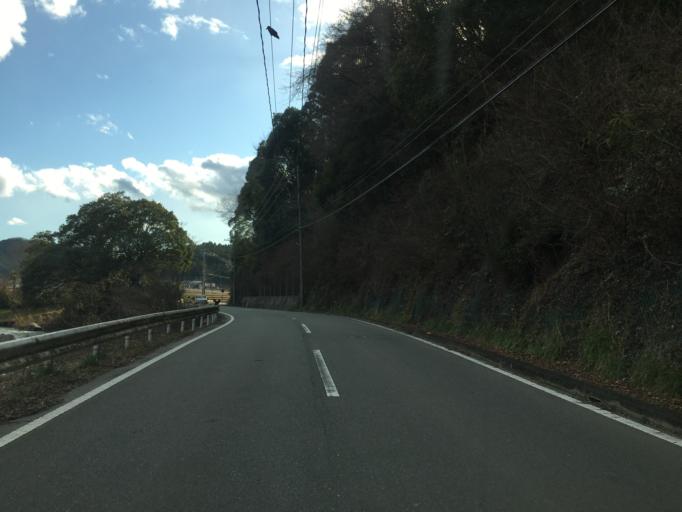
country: JP
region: Ibaraki
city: Kitaibaraki
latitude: 36.9181
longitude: 140.7356
